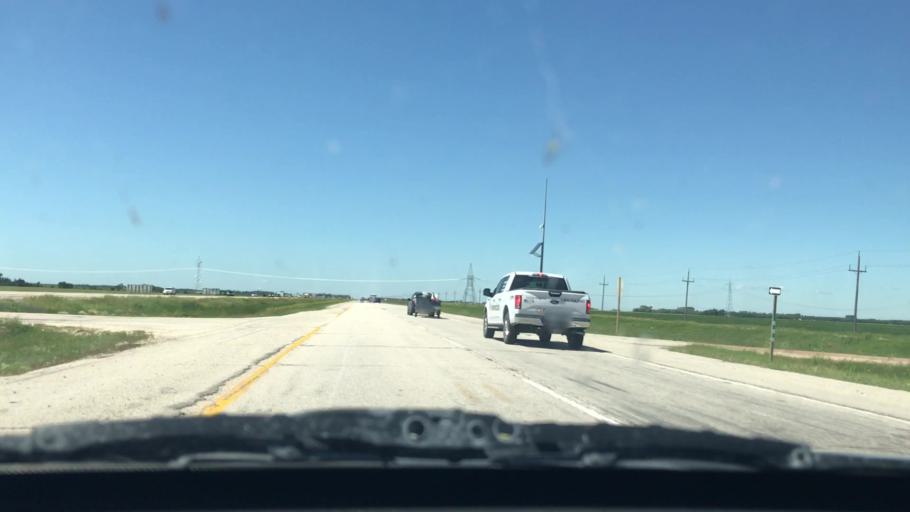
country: CA
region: Manitoba
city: Steinbach
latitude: 49.7082
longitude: -96.6636
